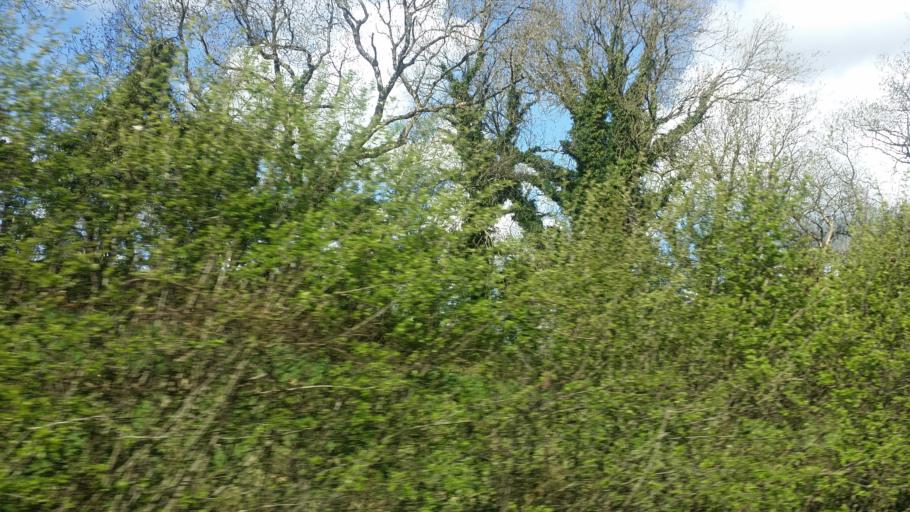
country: IE
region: Ulster
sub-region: An Cabhan
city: Virginia
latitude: 53.8517
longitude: -7.1020
